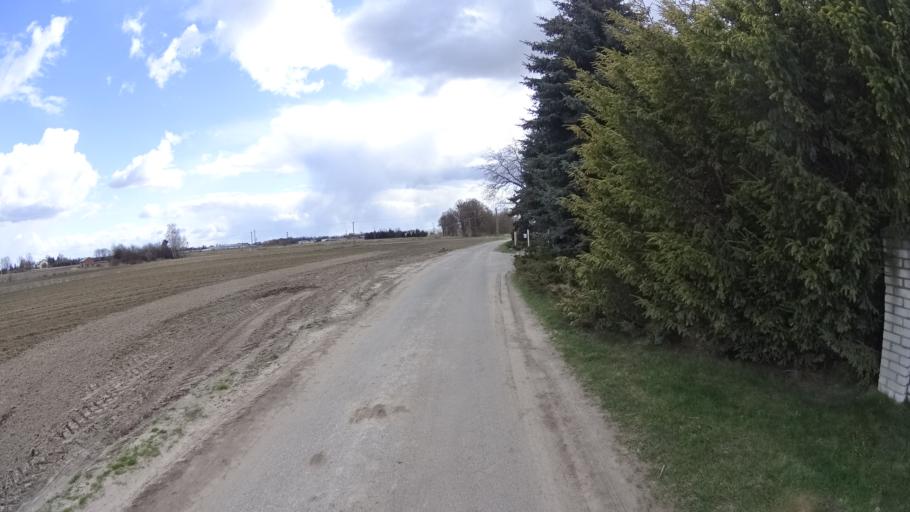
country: PL
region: Masovian Voivodeship
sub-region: Powiat warszawski zachodni
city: Jozefow
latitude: 52.2212
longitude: 20.6770
